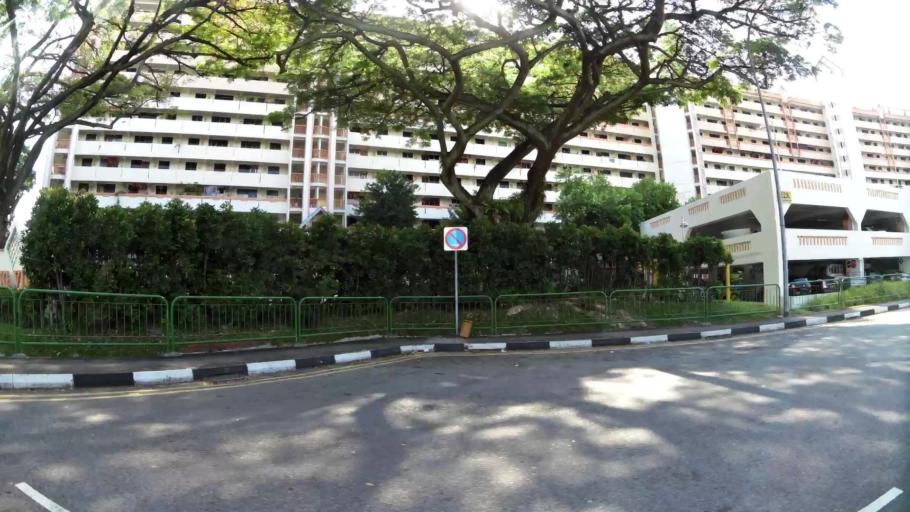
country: SG
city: Singapore
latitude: 1.3579
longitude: 103.8391
